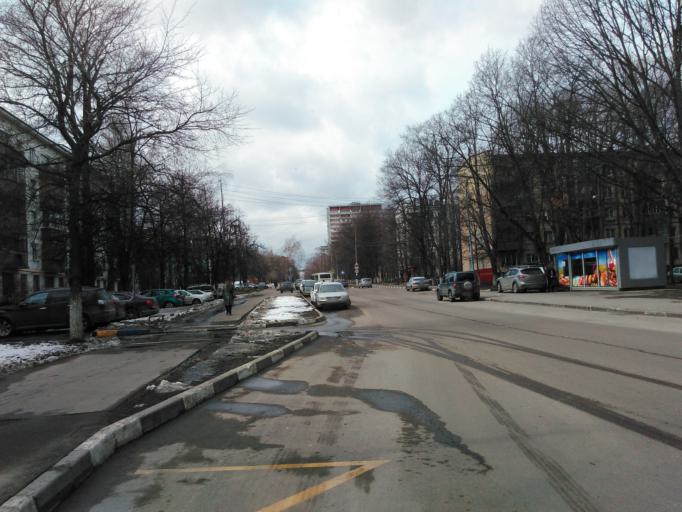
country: RU
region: Moscow
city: Zyuzino
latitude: 55.6499
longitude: 37.5772
